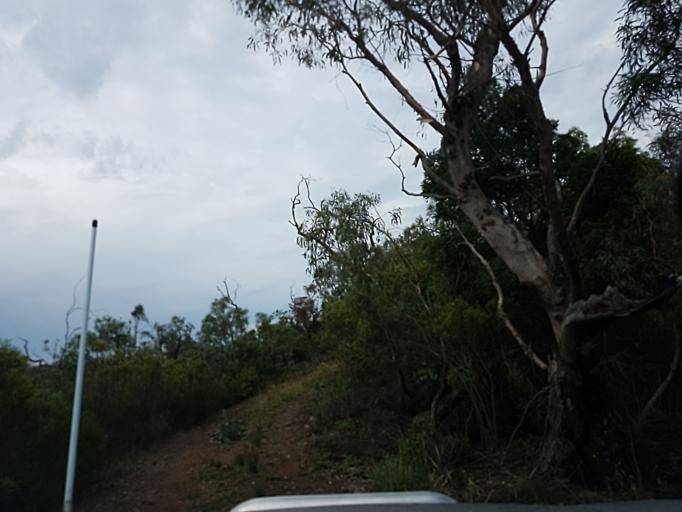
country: AU
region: New South Wales
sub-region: Snowy River
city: Jindabyne
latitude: -36.9993
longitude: 148.4031
